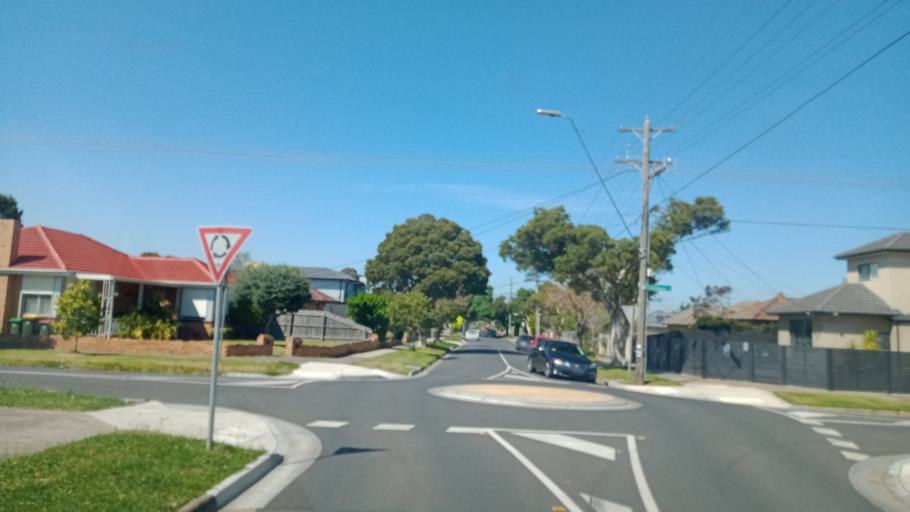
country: AU
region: Victoria
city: Murrumbeena
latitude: -37.9178
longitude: 145.0709
